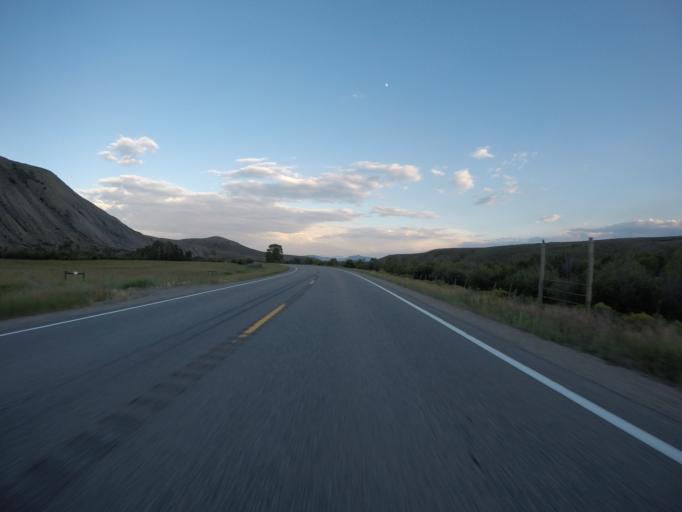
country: US
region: Colorado
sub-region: Grand County
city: Kremmling
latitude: 40.2631
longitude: -106.4595
